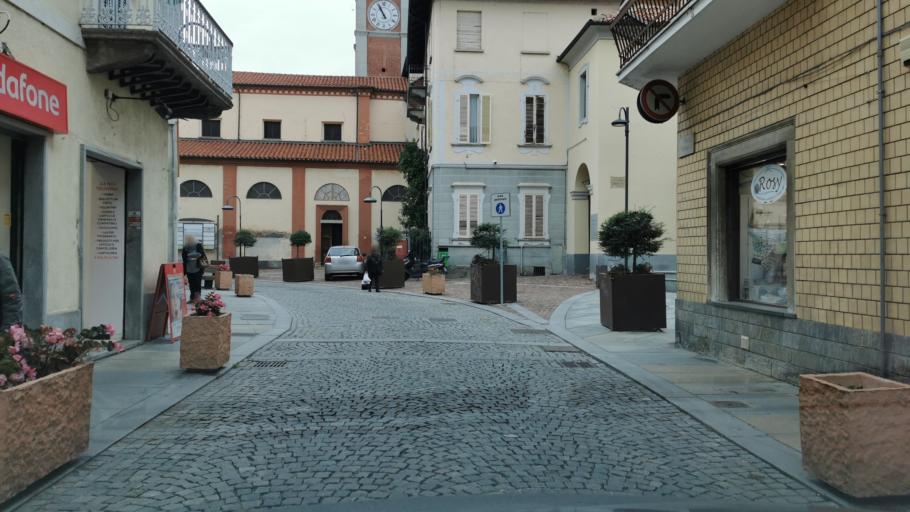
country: IT
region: Piedmont
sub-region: Provincia di Torino
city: Caselle Torinese
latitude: 45.1770
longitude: 7.6478
